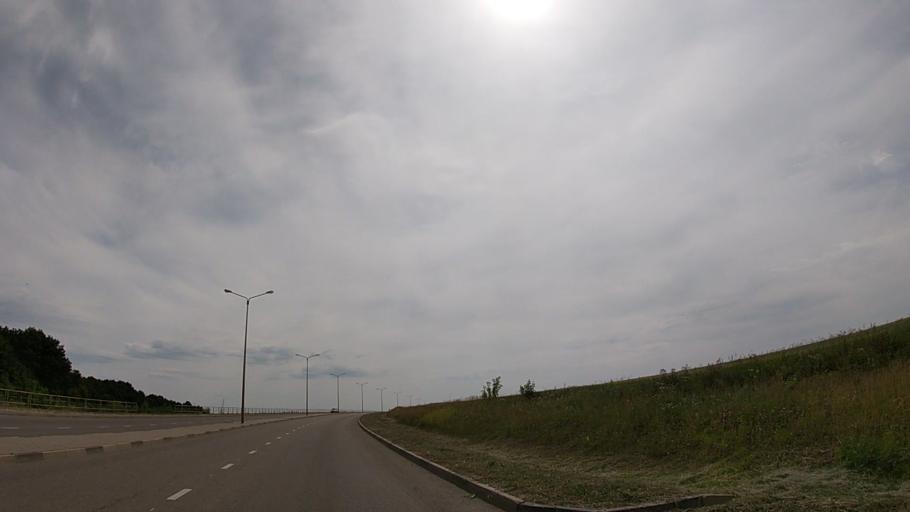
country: RU
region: Belgorod
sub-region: Belgorodskiy Rayon
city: Belgorod
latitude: 50.5948
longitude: 36.5225
